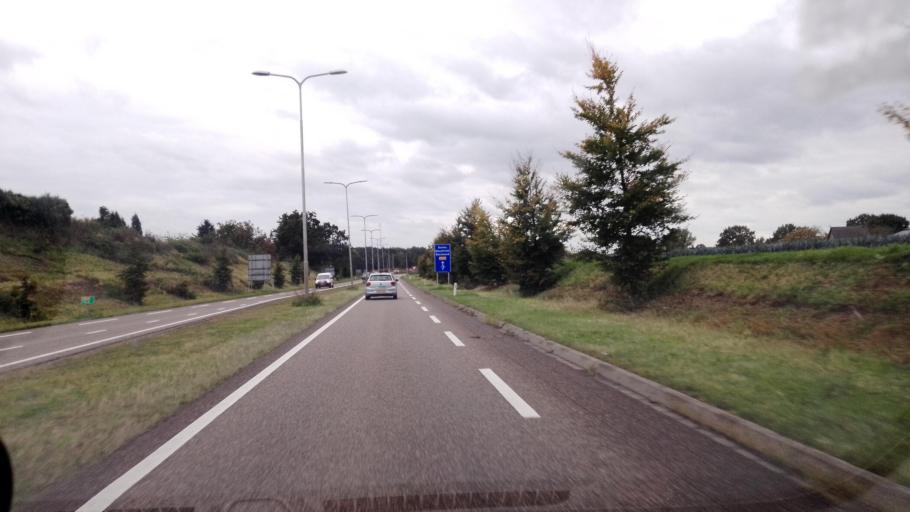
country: NL
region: Limburg
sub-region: Gemeente Venlo
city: Tegelen
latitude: 51.3617
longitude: 6.1223
